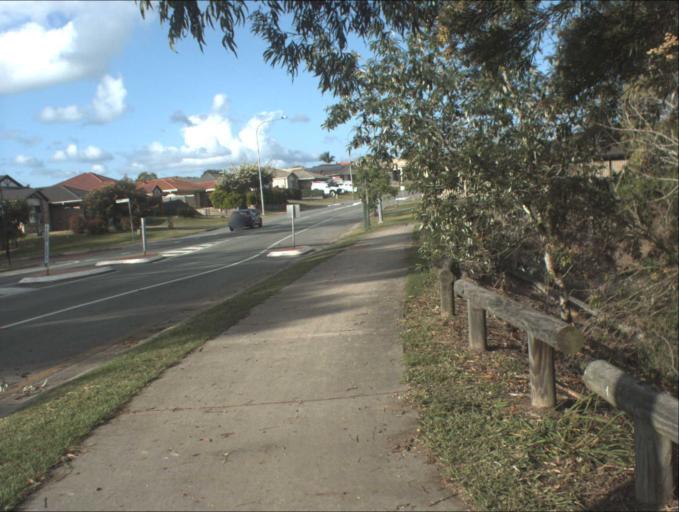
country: AU
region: Queensland
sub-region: Logan
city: Park Ridge South
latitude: -27.6819
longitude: 153.0528
